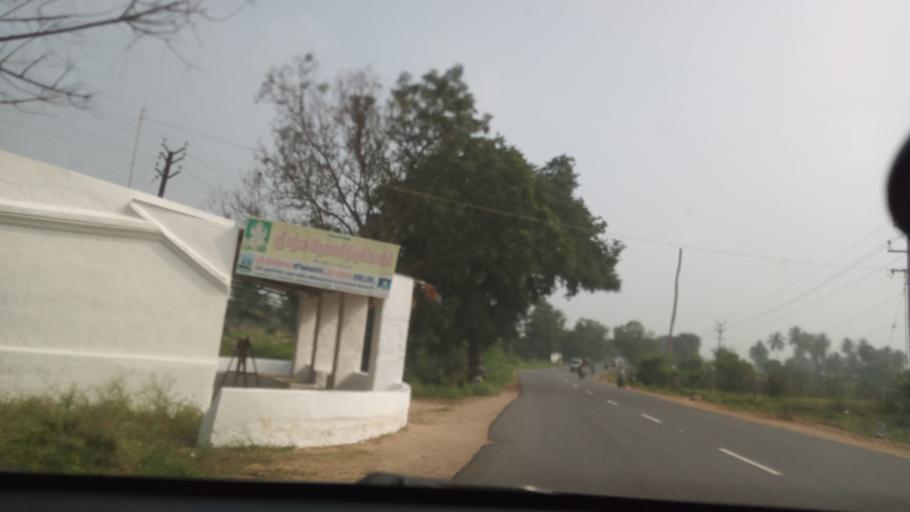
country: IN
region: Tamil Nadu
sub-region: Erode
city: Punjai Puliyampatti
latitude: 11.3290
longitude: 77.1511
